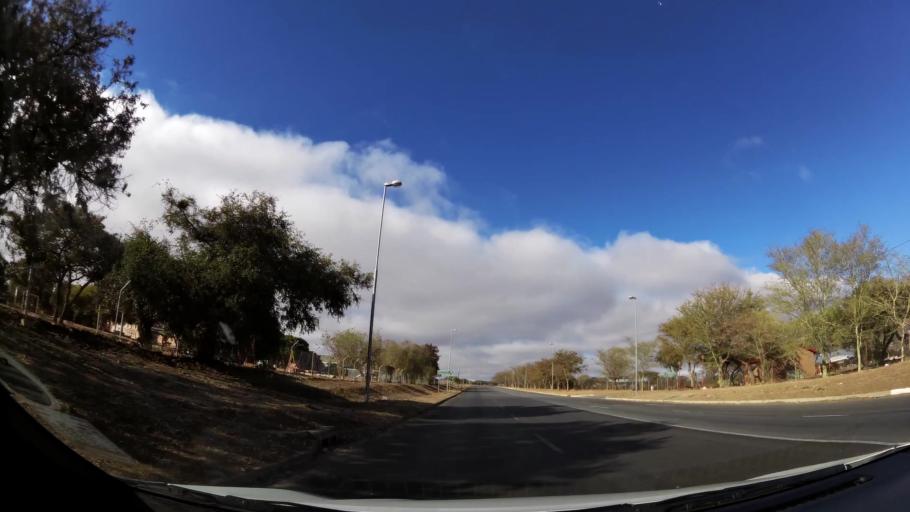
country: ZA
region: Limpopo
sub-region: Capricorn District Municipality
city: Polokwane
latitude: -23.9167
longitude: 29.4759
